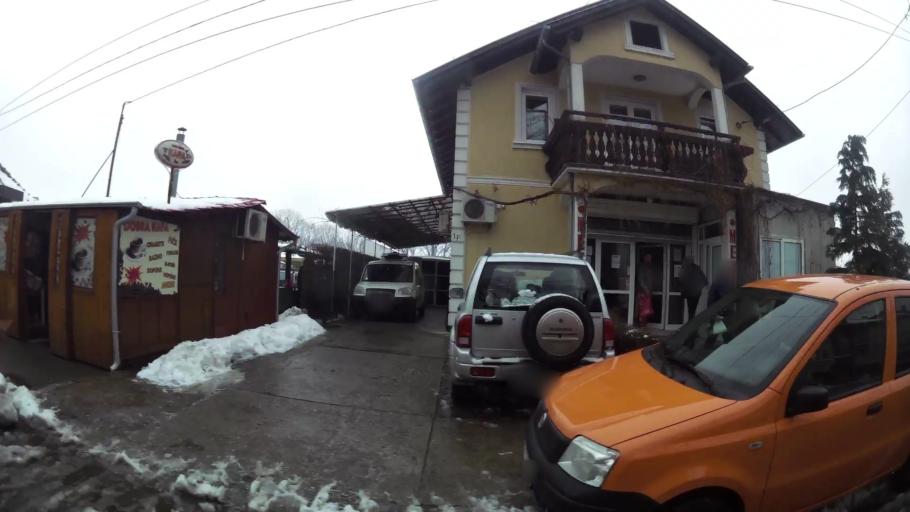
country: RS
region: Central Serbia
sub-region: Belgrade
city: Zemun
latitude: 44.8714
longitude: 20.3254
